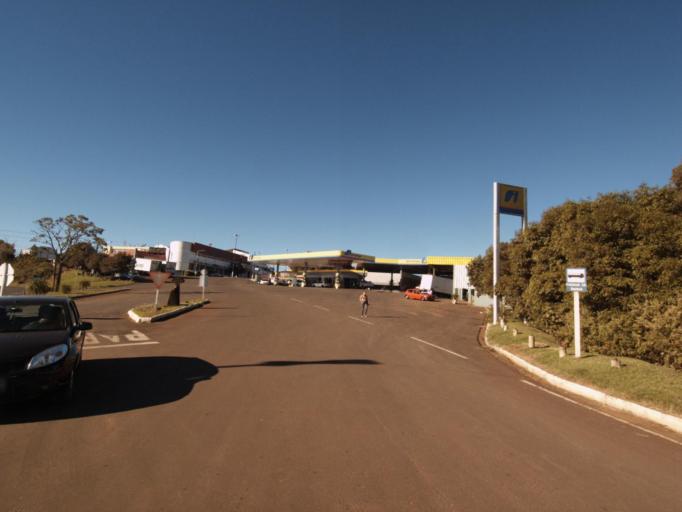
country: BR
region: Santa Catarina
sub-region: Chapeco
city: Chapeco
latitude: -26.9867
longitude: -52.6052
